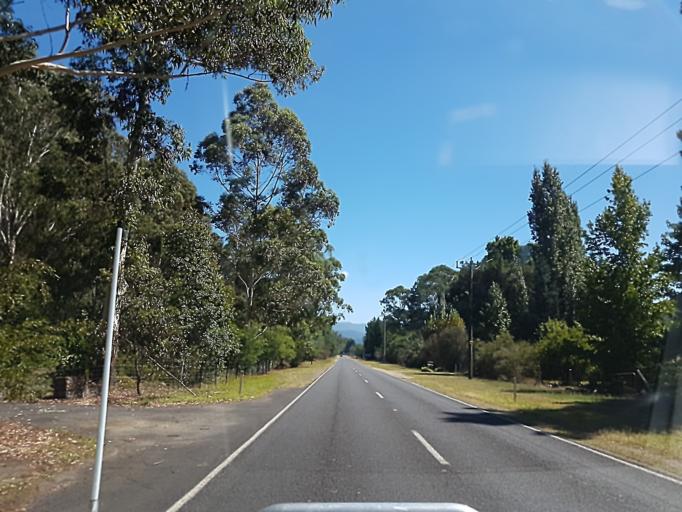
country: AU
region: Victoria
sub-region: Alpine
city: Mount Beauty
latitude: -36.7774
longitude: 147.0326
